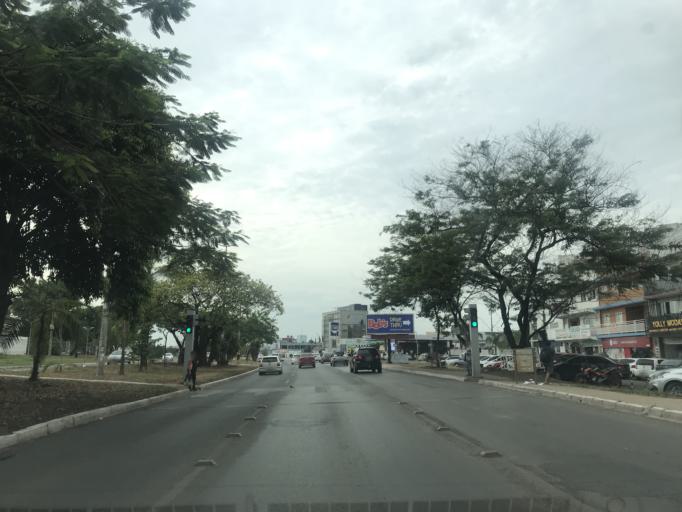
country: BR
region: Federal District
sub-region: Brasilia
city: Brasilia
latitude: -15.8432
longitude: -47.9824
